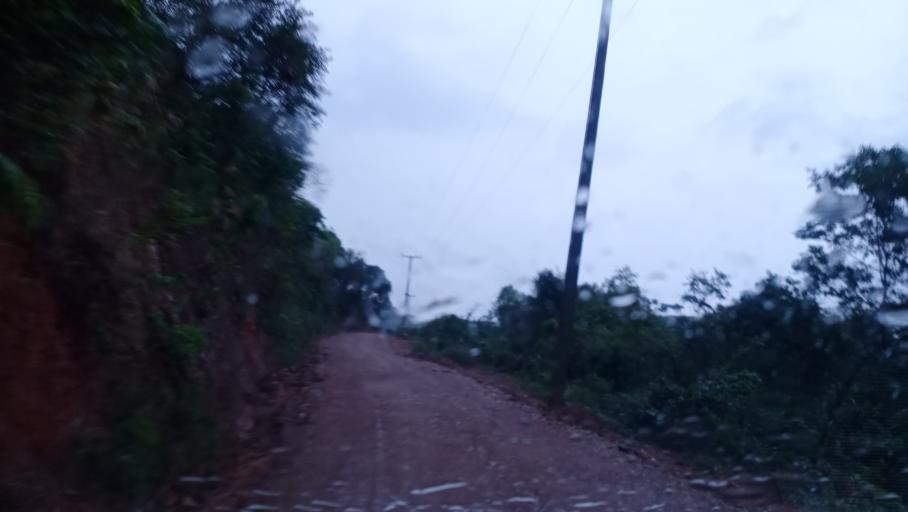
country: LA
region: Phongsali
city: Khoa
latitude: 21.1869
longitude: 102.3360
